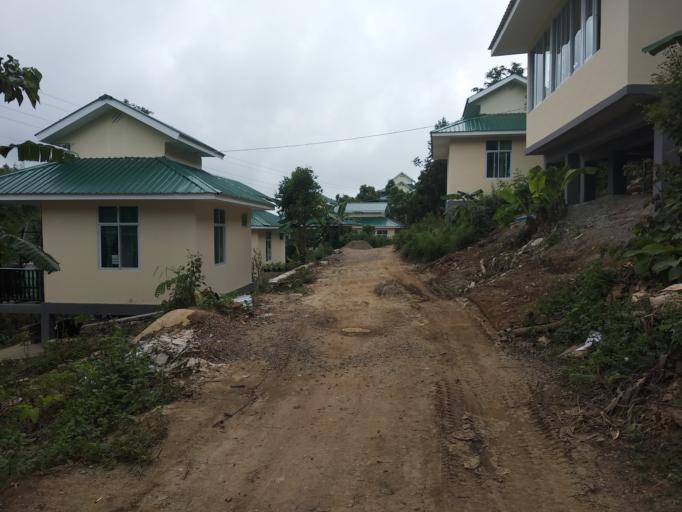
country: MM
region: Mandalay
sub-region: Pyin Oo Lwin District
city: Pyin Oo Lwin
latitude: 21.9155
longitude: 96.3863
